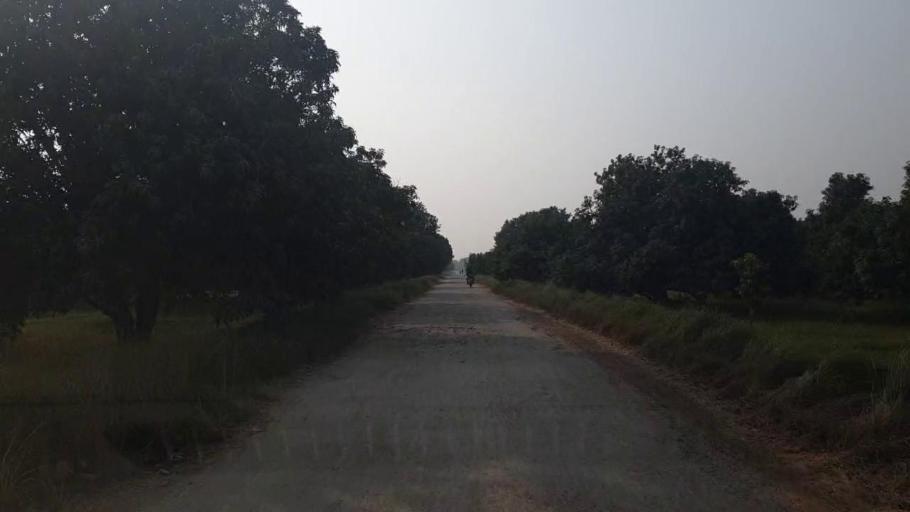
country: PK
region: Sindh
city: Tando Jam
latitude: 25.3292
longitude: 68.5180
